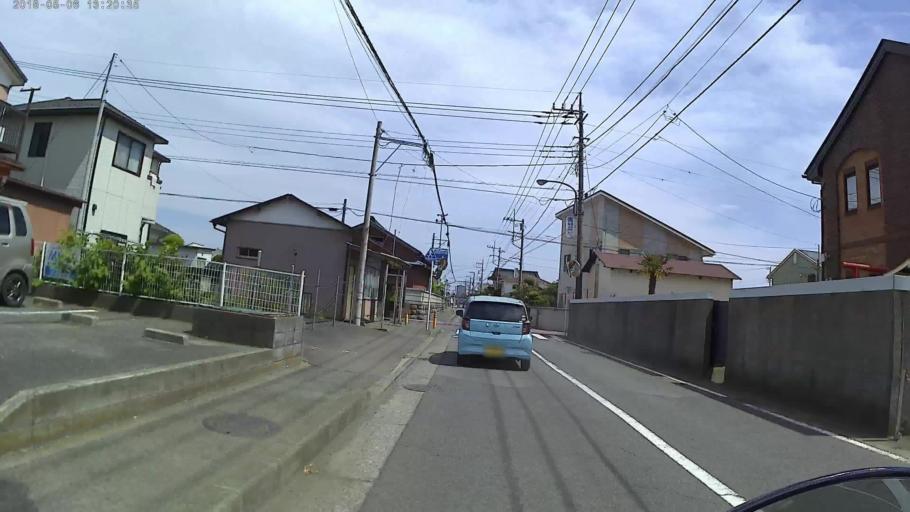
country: JP
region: Kanagawa
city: Minami-rinkan
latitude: 35.4110
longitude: 139.4454
